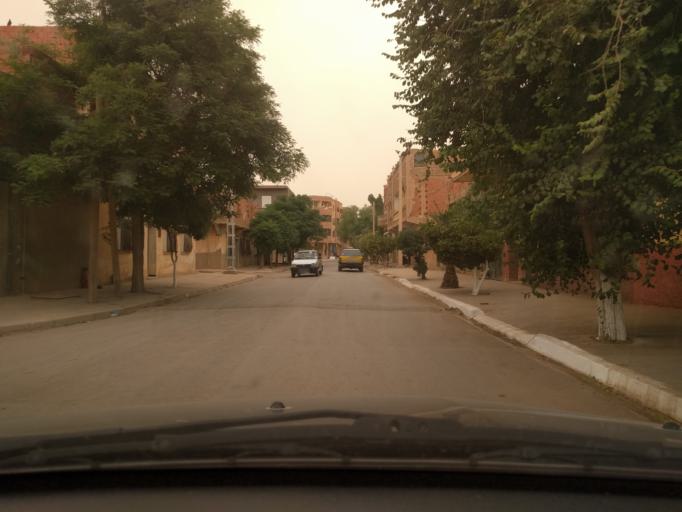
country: DZ
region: Tiaret
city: Frenda
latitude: 35.0632
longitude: 1.0638
